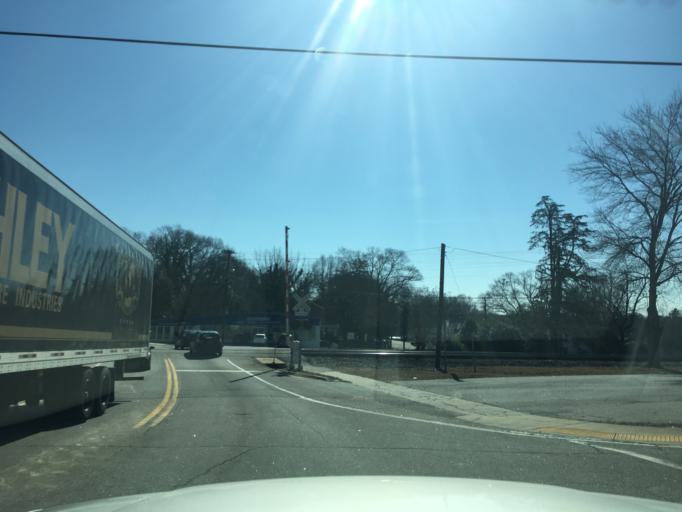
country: US
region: South Carolina
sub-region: Pickens County
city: Liberty
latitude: 34.7866
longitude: -82.6925
